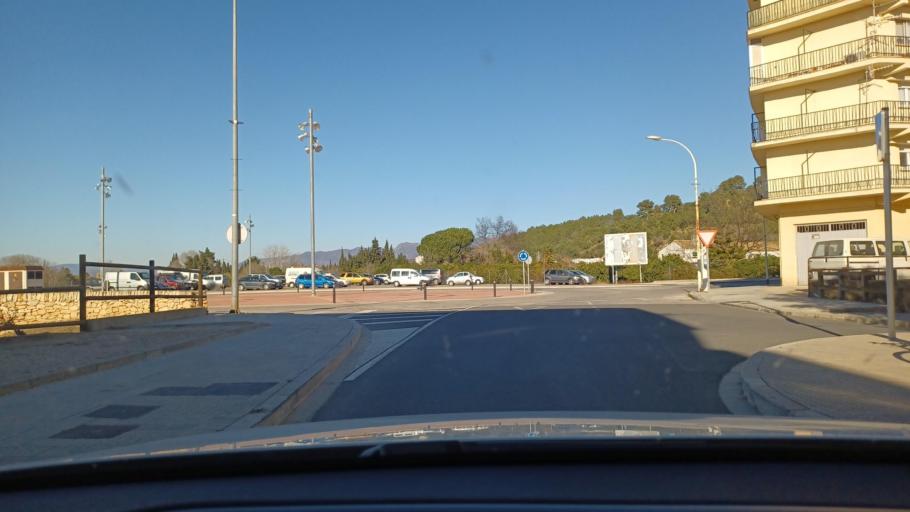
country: ES
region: Catalonia
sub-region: Provincia de Tarragona
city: Tortosa
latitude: 40.8197
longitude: 0.5240
